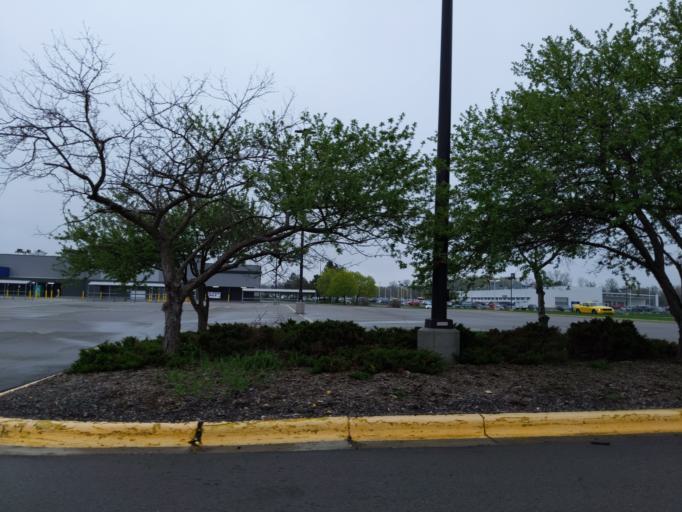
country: US
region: Michigan
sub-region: Ingham County
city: Holt
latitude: 42.6625
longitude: -84.5479
